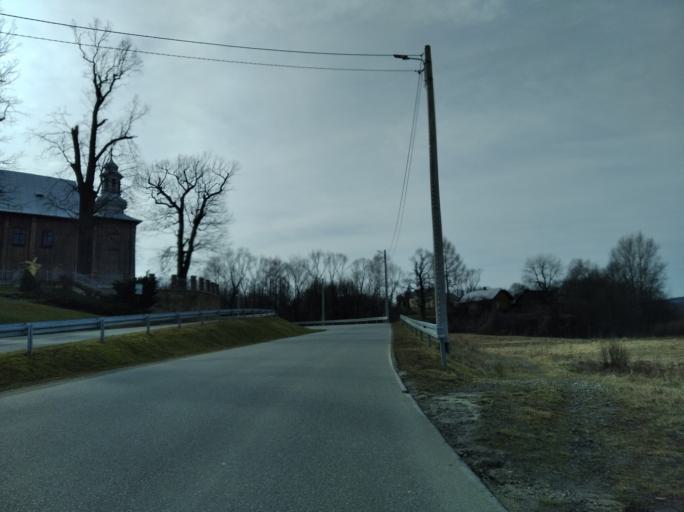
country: PL
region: Subcarpathian Voivodeship
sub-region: Powiat brzozowski
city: Jasienica Rosielna
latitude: 49.7495
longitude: 21.9416
